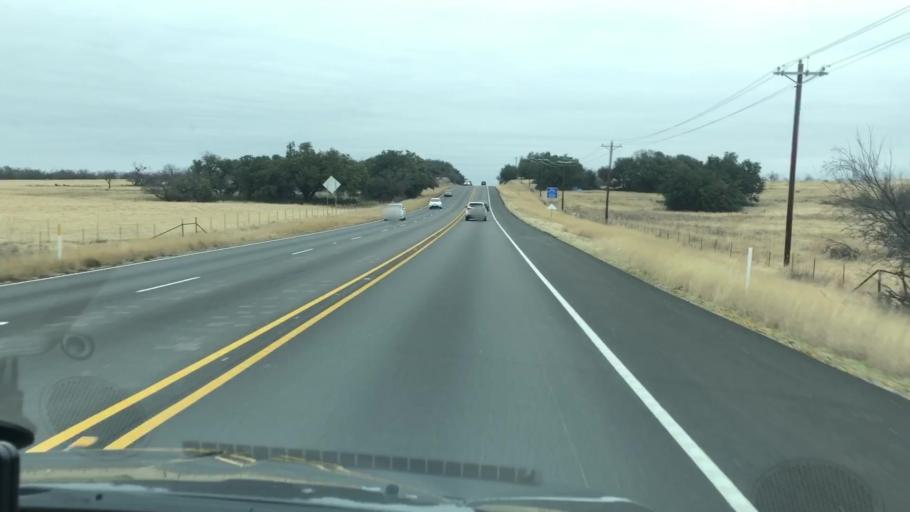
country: US
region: Texas
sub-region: Erath County
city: Stephenville
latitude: 32.3023
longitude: -98.1872
